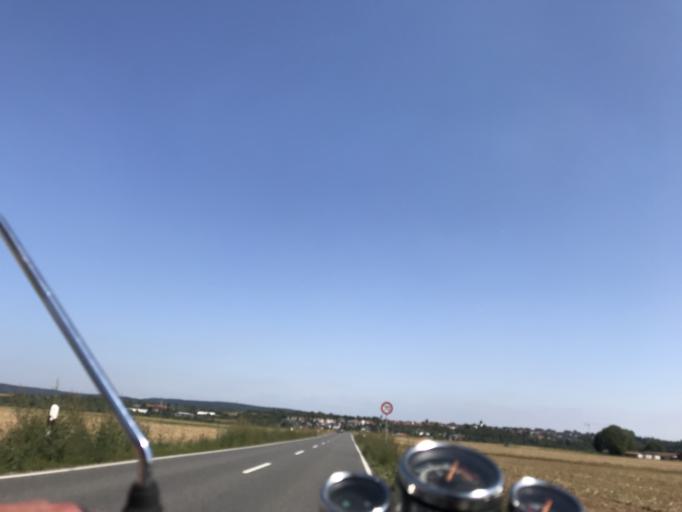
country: DE
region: Hesse
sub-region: Regierungsbezirk Darmstadt
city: Wiesbaden
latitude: 50.0819
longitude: 8.3050
